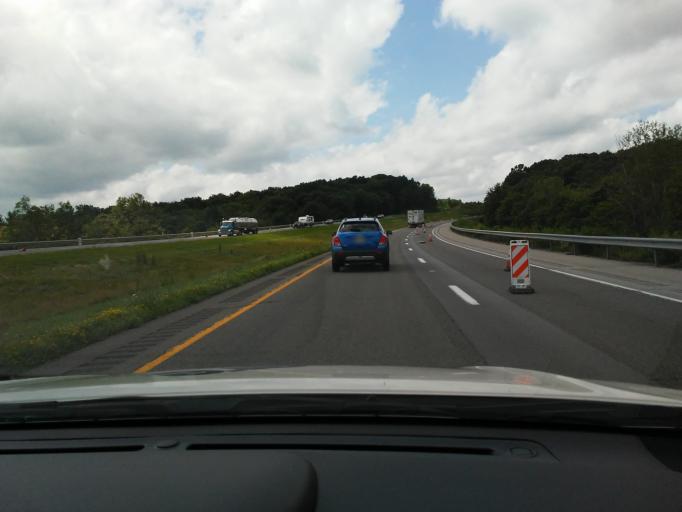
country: US
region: Pennsylvania
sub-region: Venango County
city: Seneca
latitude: 41.1869
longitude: -79.7938
